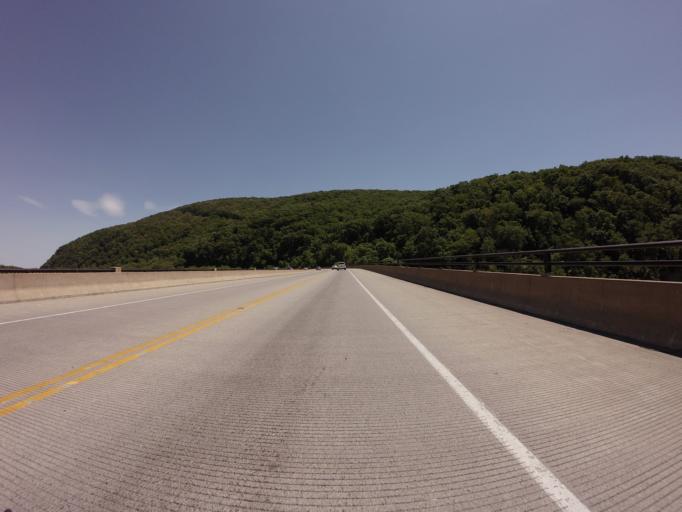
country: US
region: West Virginia
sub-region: Jefferson County
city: Bolivar
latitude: 39.3202
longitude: -77.7420
